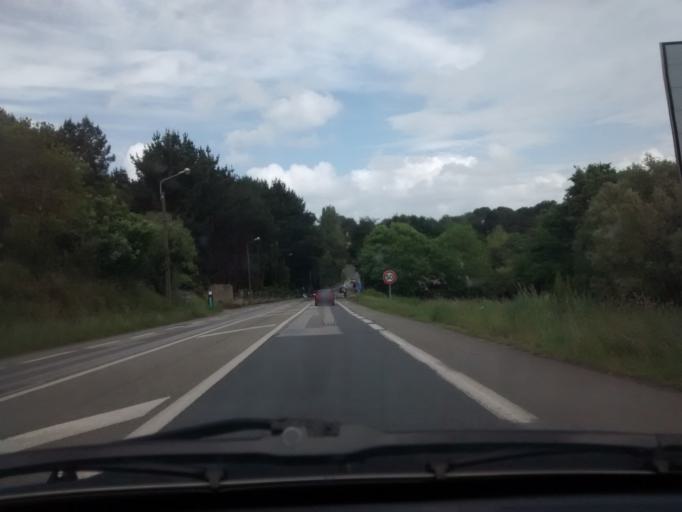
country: FR
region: Brittany
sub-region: Departement du Morbihan
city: Arradon
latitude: 47.6485
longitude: -2.8007
